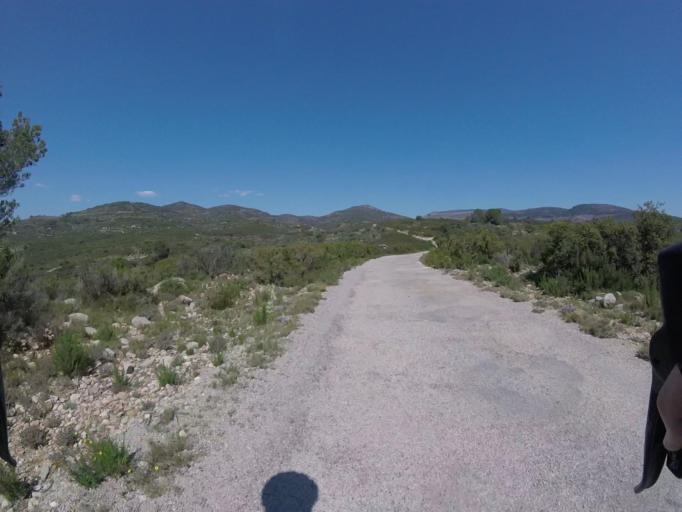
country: ES
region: Valencia
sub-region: Provincia de Castello
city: Sierra-Engarceran
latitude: 40.2352
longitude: -0.0263
